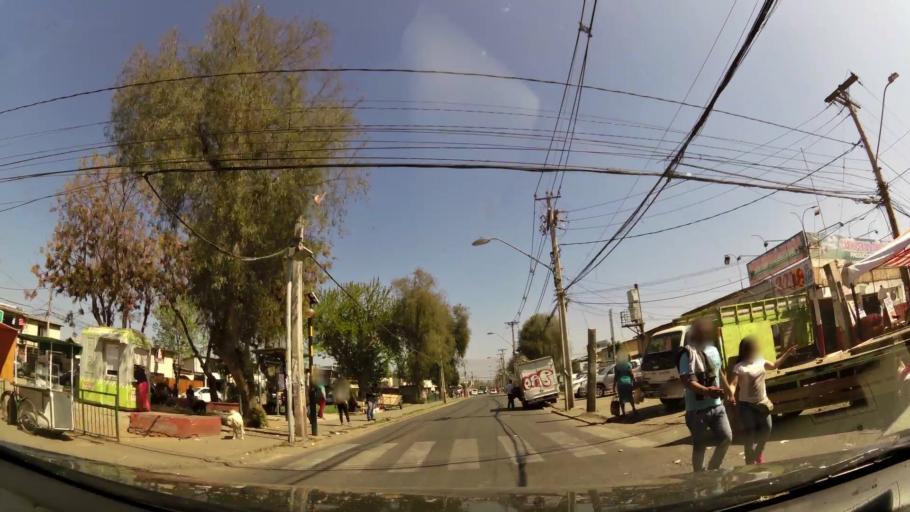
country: CL
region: Santiago Metropolitan
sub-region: Provincia de Santiago
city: Lo Prado
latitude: -33.3618
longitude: -70.7442
